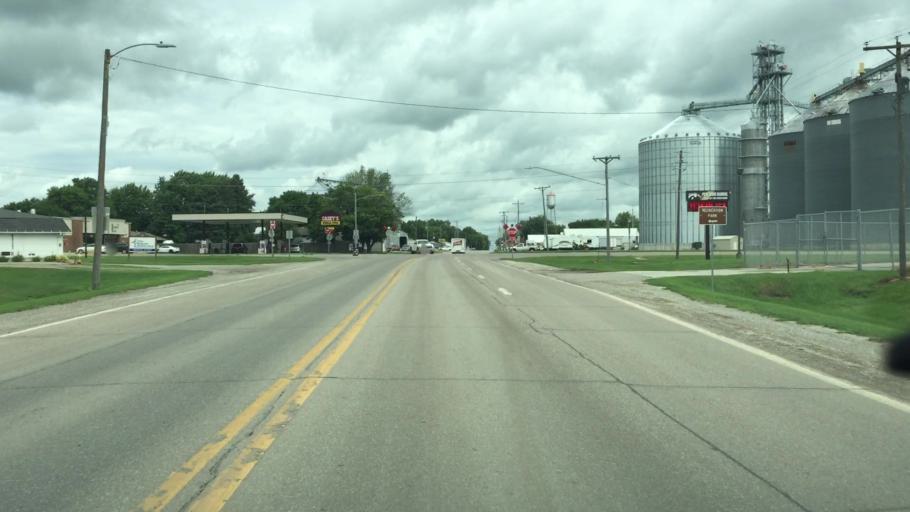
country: US
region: Iowa
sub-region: Jasper County
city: Monroe
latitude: 41.5163
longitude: -93.1016
